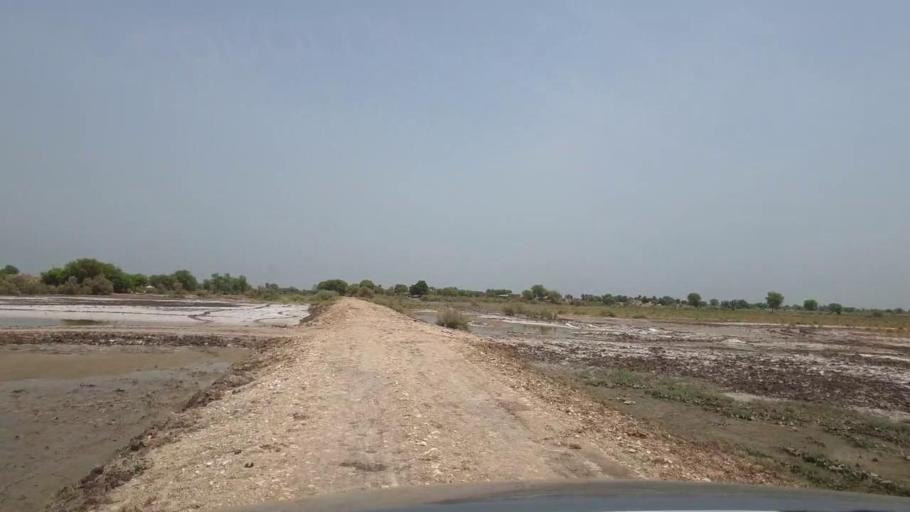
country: PK
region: Sindh
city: Madeji
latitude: 27.7638
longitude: 68.3788
